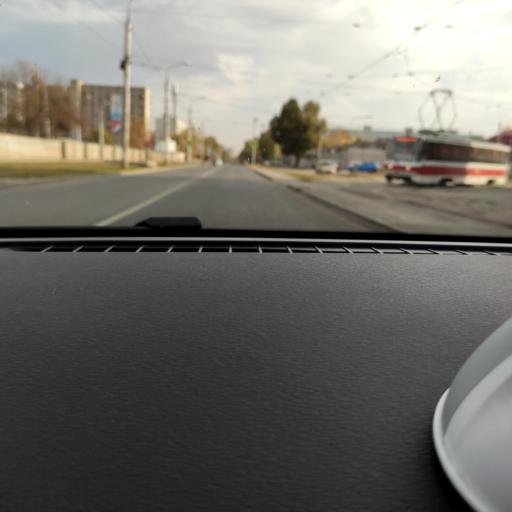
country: RU
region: Samara
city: Samara
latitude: 53.2330
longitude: 50.2042
